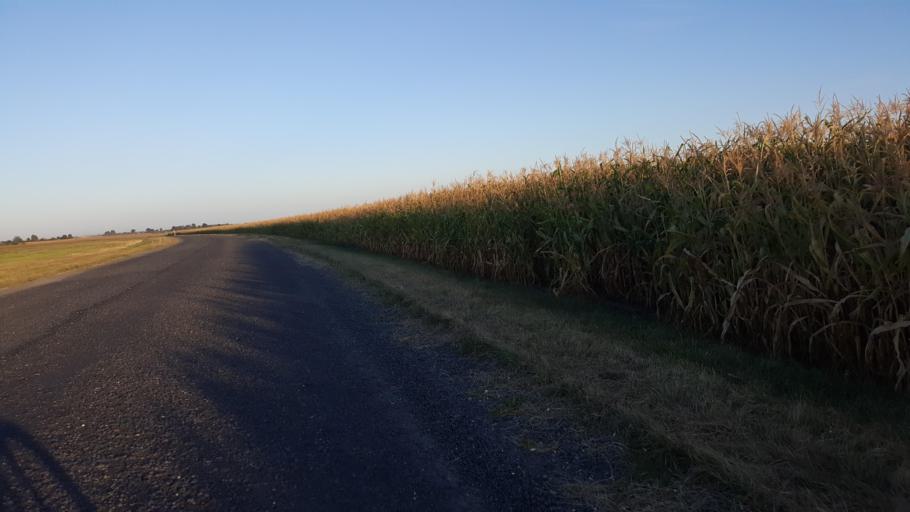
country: BY
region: Brest
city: Vysokaye
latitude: 52.2983
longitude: 23.5007
